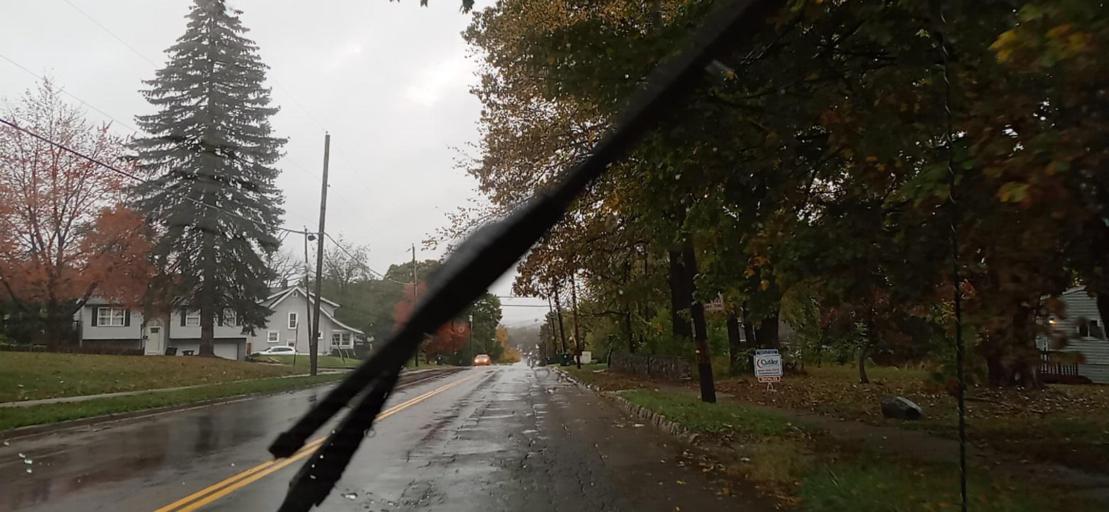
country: US
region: Ohio
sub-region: Summit County
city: Akron
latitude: 41.0544
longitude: -81.5633
